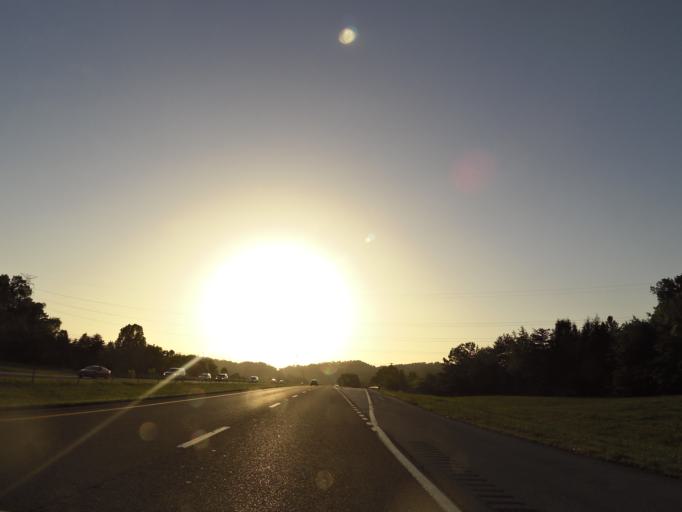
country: US
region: Tennessee
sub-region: Blount County
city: Alcoa
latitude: 35.8435
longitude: -83.9868
